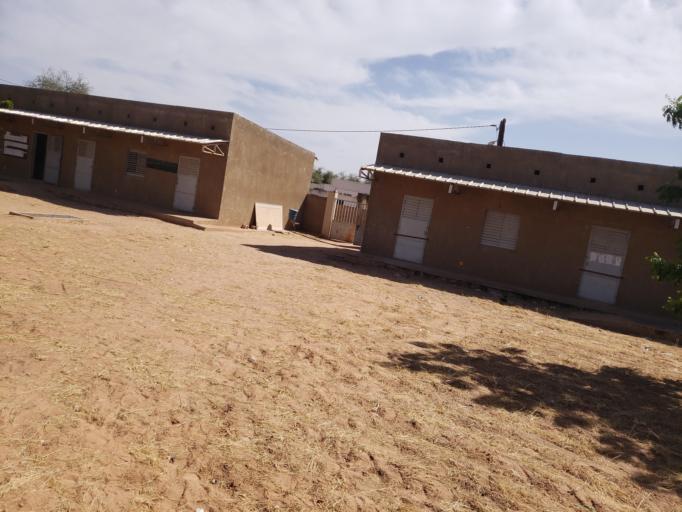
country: SN
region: Matam
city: Ranerou
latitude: 15.3001
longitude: -13.9679
